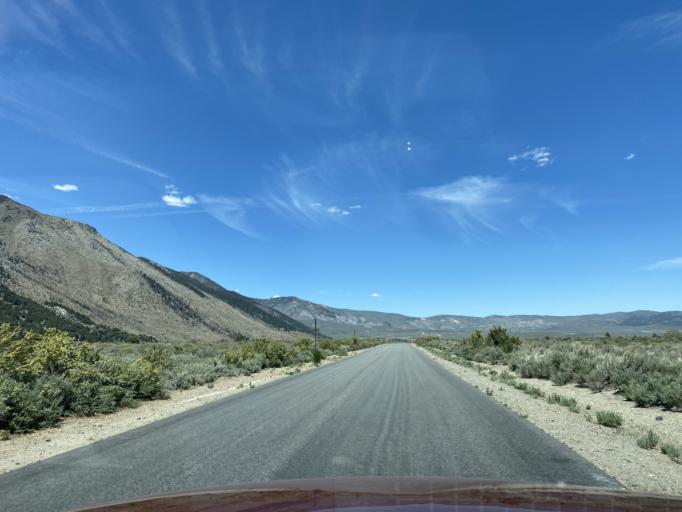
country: US
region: California
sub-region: Mono County
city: Bridgeport
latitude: 37.9621
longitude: -119.1204
